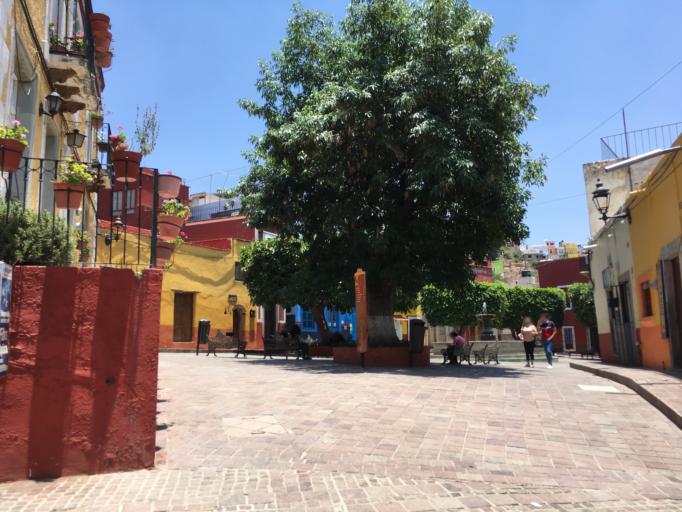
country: MX
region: Guanajuato
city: Guanajuato
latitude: 21.0155
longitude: -101.2513
